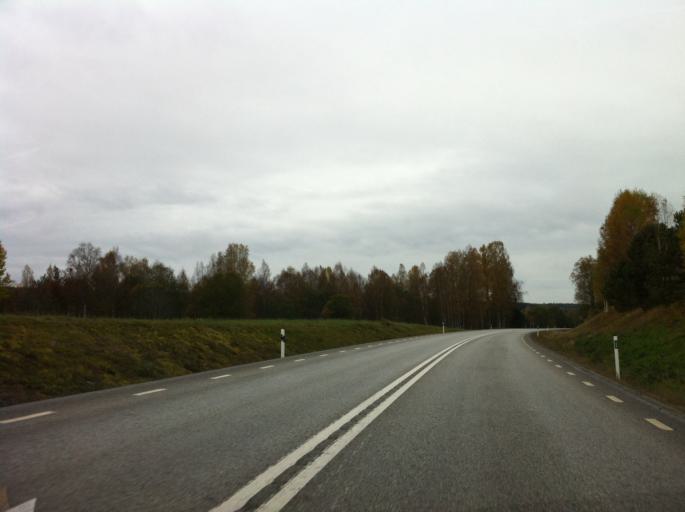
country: SE
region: OErebro
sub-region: Ljusnarsbergs Kommun
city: Kopparberg
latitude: 59.8391
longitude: 15.0899
